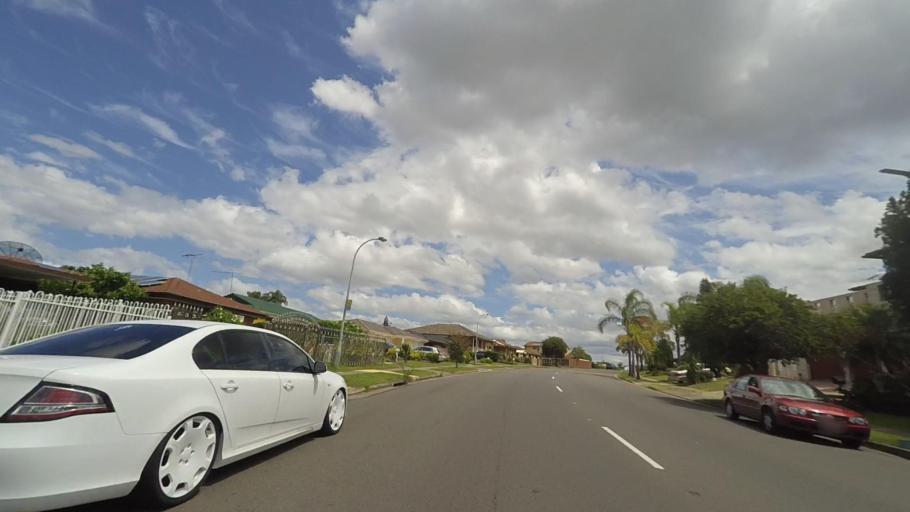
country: AU
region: New South Wales
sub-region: Fairfield
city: Cabramatta West
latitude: -33.8723
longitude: 150.9106
